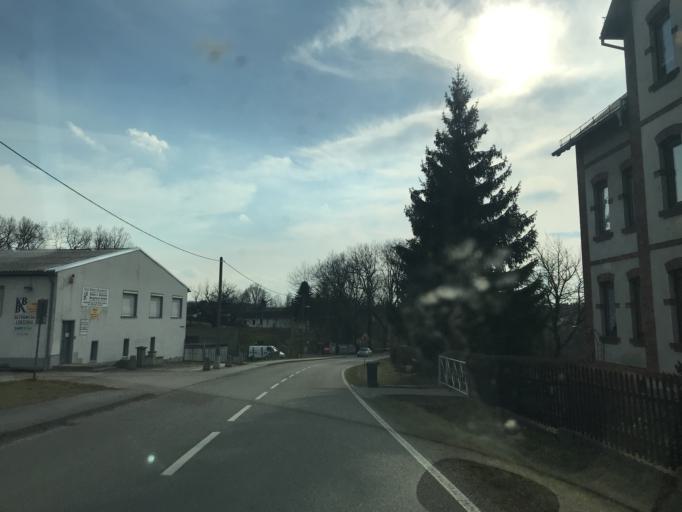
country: DE
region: Saxony
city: Lunzenau
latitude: 50.9684
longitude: 12.7640
